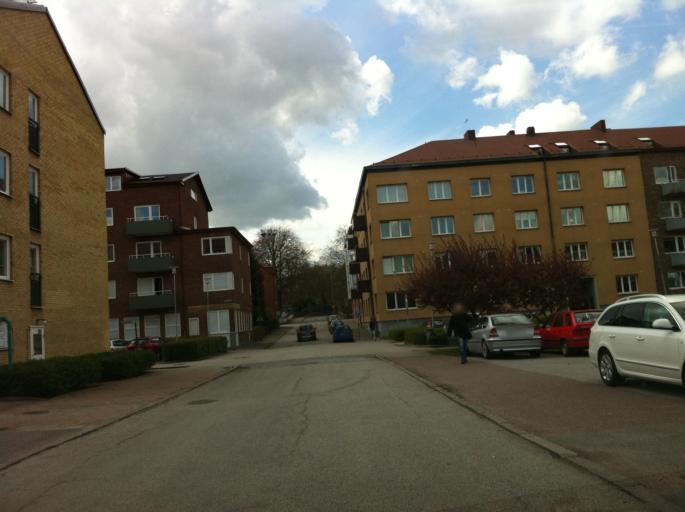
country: SE
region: Skane
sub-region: Eslovs Kommun
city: Eslov
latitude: 55.8366
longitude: 13.3024
